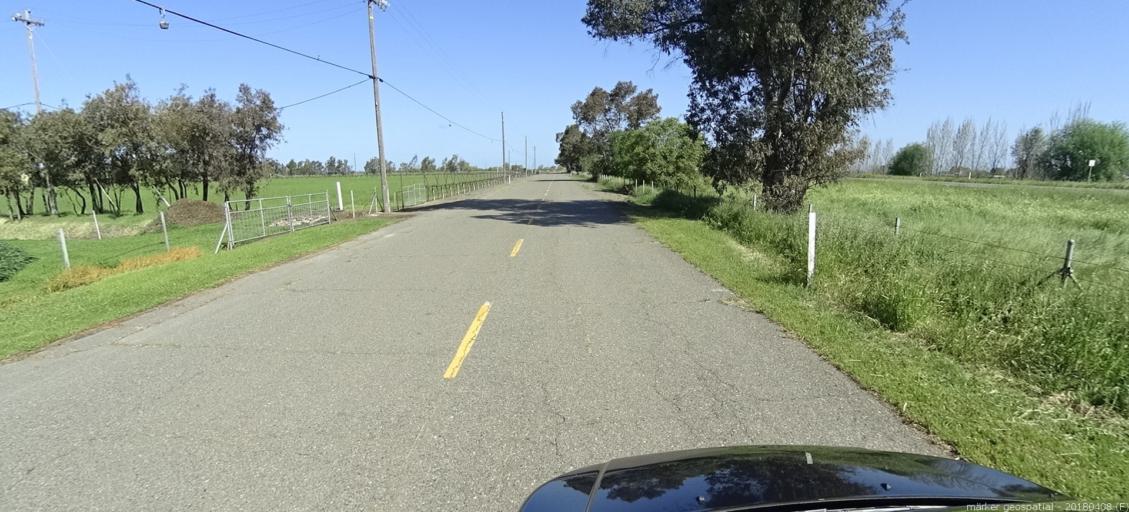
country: US
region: California
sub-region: Sacramento County
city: Laguna
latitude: 38.3333
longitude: -121.4687
